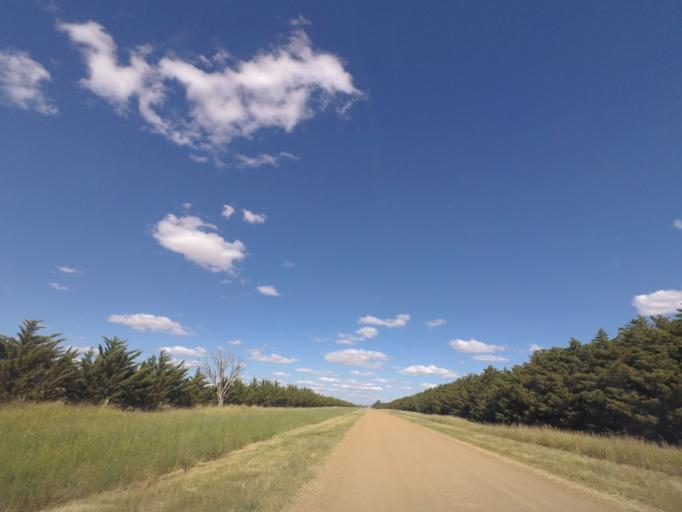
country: AU
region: Victoria
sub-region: Hume
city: Sunbury
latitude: -37.4587
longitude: 144.7895
